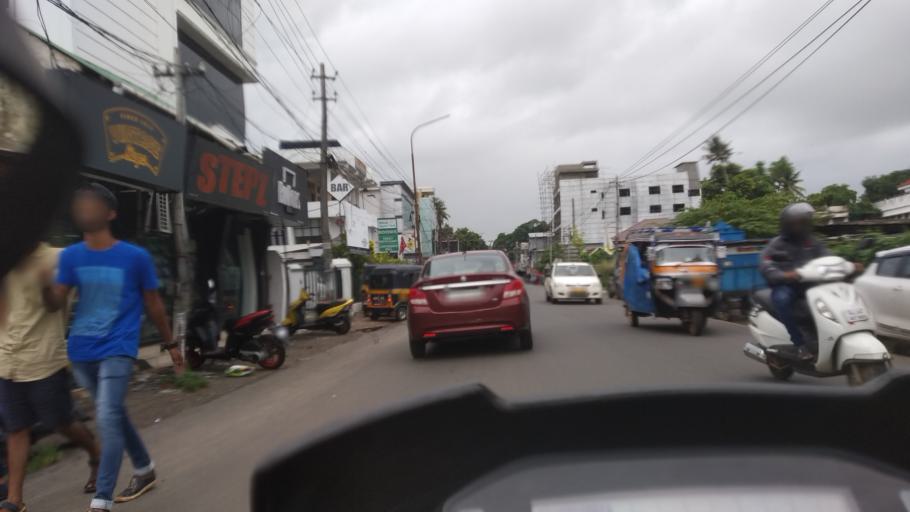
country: IN
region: Kerala
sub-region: Alappuzha
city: Alleppey
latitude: 9.4985
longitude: 76.3388
